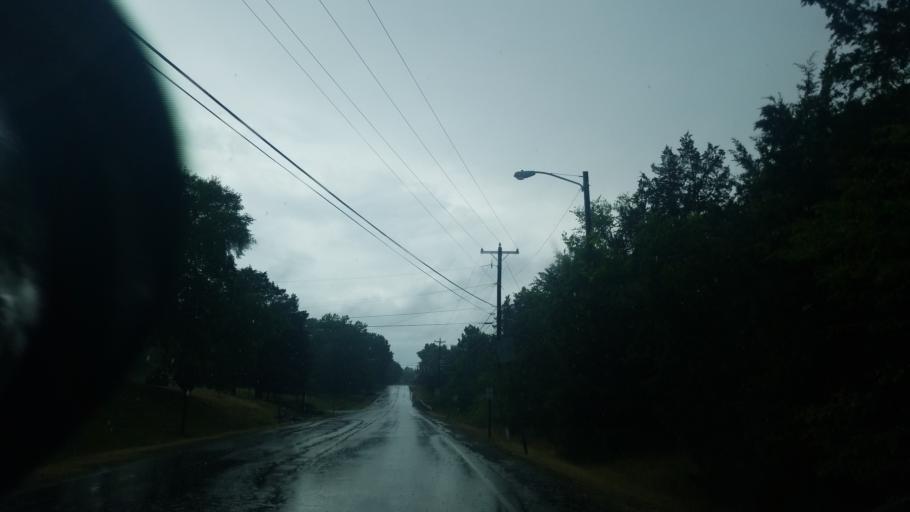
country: US
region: Tennessee
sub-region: Rutherford County
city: La Vergne
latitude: 36.1076
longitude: -86.6017
